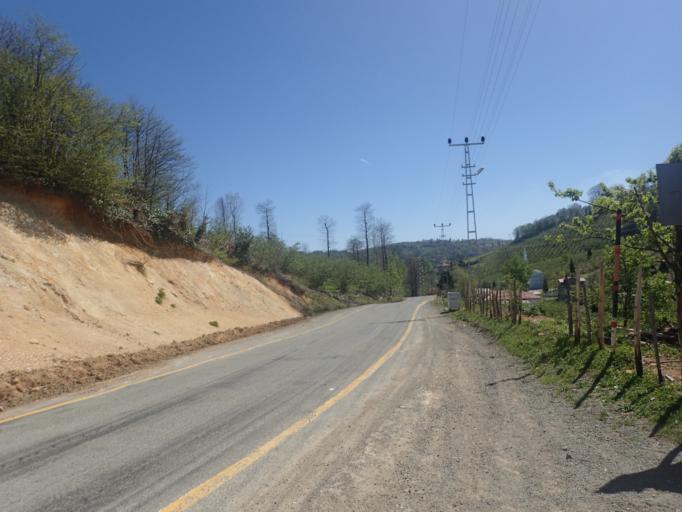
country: TR
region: Ordu
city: Kabaduz
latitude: 40.7978
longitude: 37.9129
